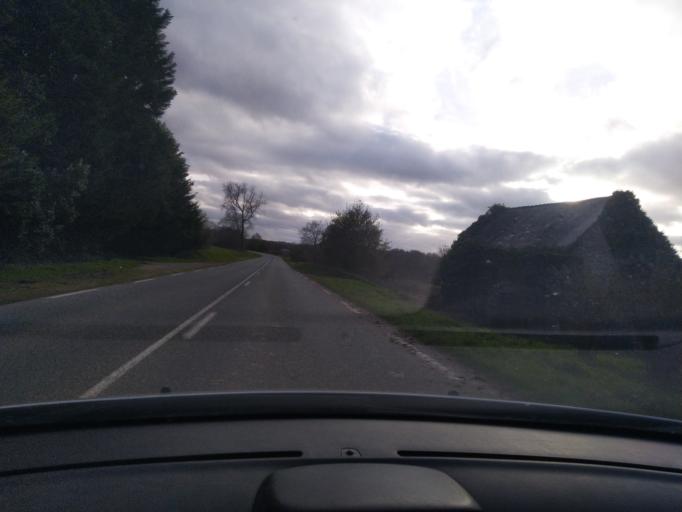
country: FR
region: Brittany
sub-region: Departement des Cotes-d'Armor
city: Plouaret
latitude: 48.5934
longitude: -3.4950
